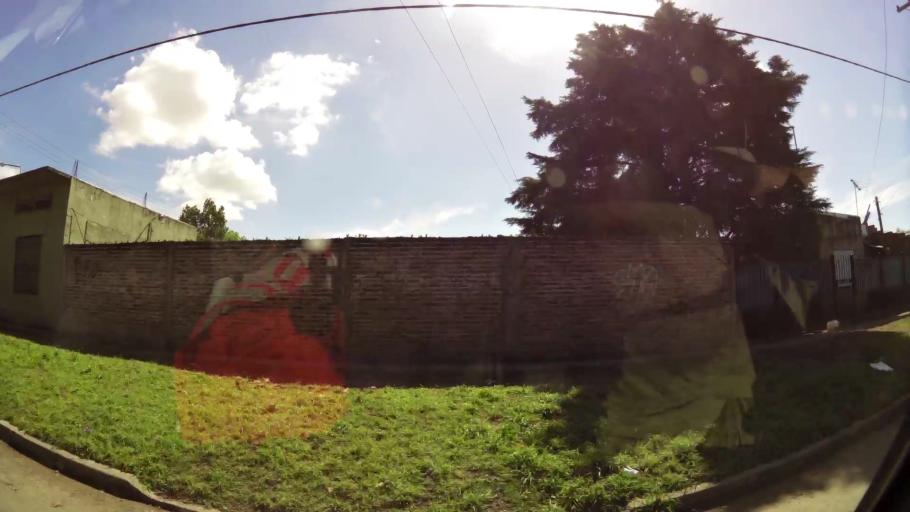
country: AR
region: Buenos Aires
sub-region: Partido de Quilmes
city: Quilmes
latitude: -34.8021
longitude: -58.2699
